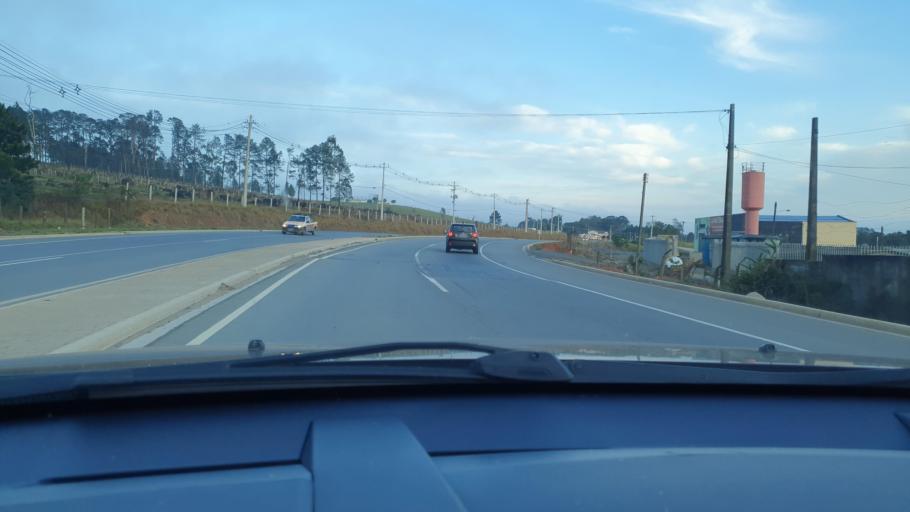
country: BR
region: Sao Paulo
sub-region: Ibiuna
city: Ibiuna
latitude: -23.6554
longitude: -47.1194
